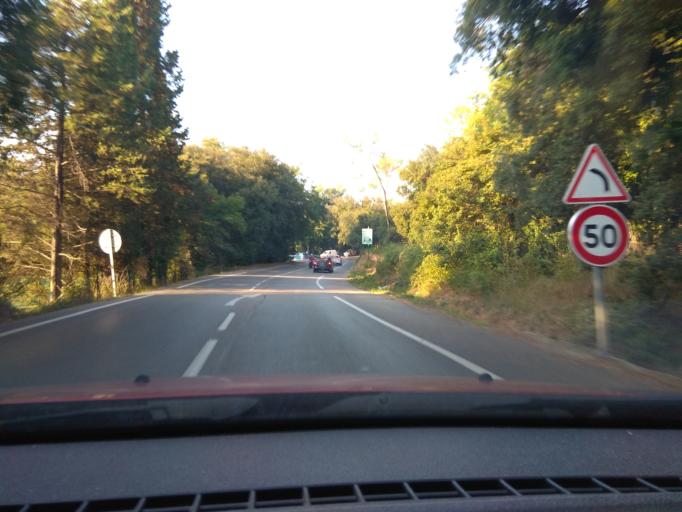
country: FR
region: Provence-Alpes-Cote d'Azur
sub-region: Departement des Alpes-Maritimes
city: Le Rouret
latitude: 43.6561
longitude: 7.0263
